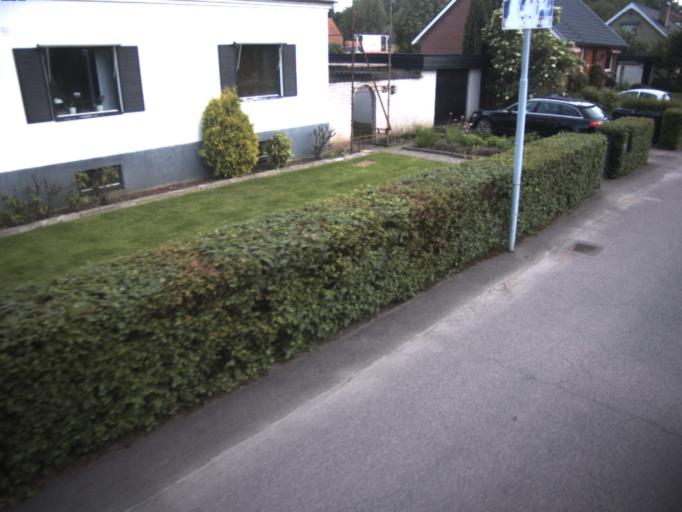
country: SE
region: Skane
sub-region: Helsingborg
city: Odakra
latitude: 56.1023
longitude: 12.7436
